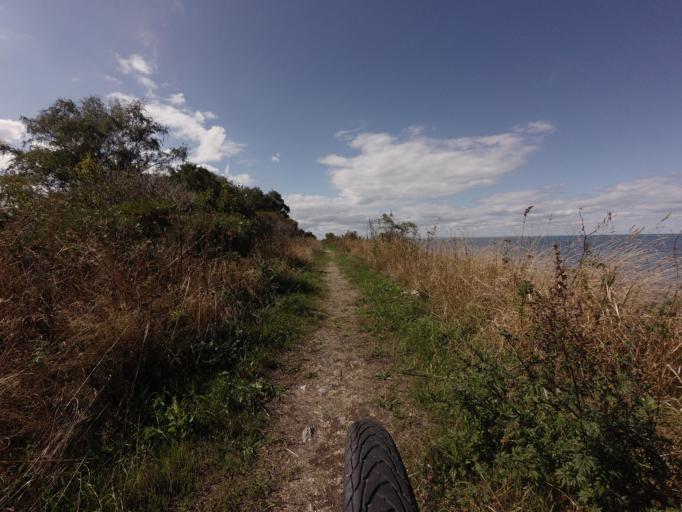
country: DK
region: Zealand
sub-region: Vordingborg Kommune
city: Stege
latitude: 55.0234
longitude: 12.4452
